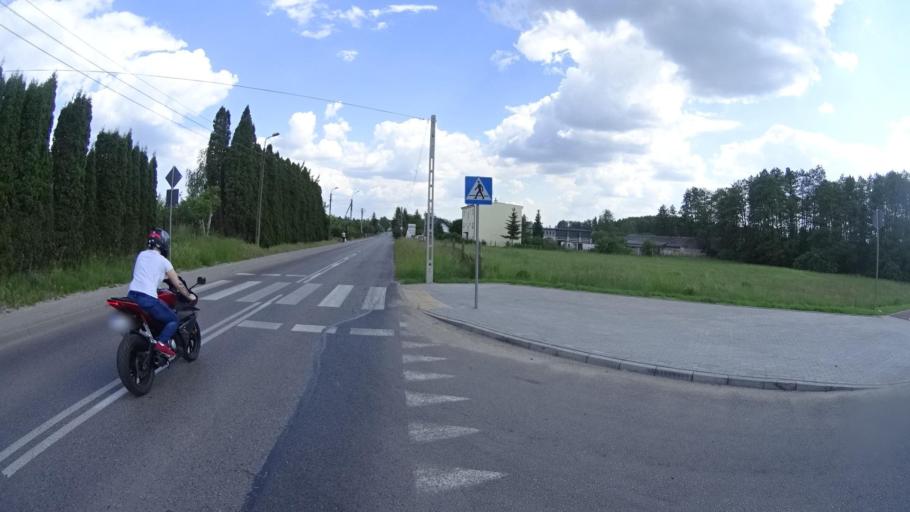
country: PL
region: Masovian Voivodeship
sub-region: Powiat piaseczynski
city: Tarczyn
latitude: 51.9881
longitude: 20.8254
